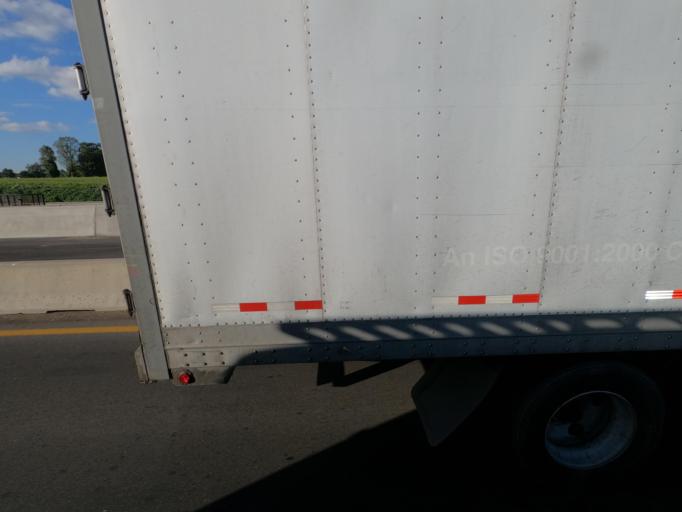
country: US
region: Tennessee
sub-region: Madison County
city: Jackson
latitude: 35.6804
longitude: -88.7694
